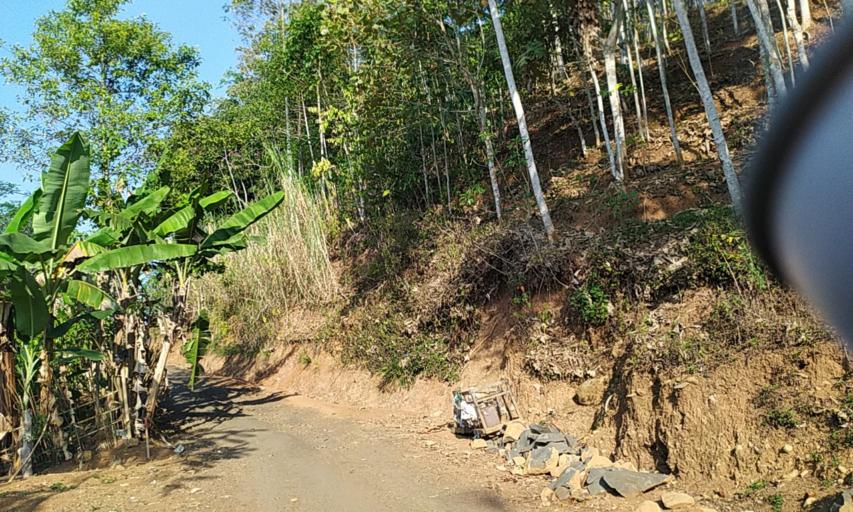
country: ID
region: Central Java
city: Datar
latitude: -7.2267
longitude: 108.6350
